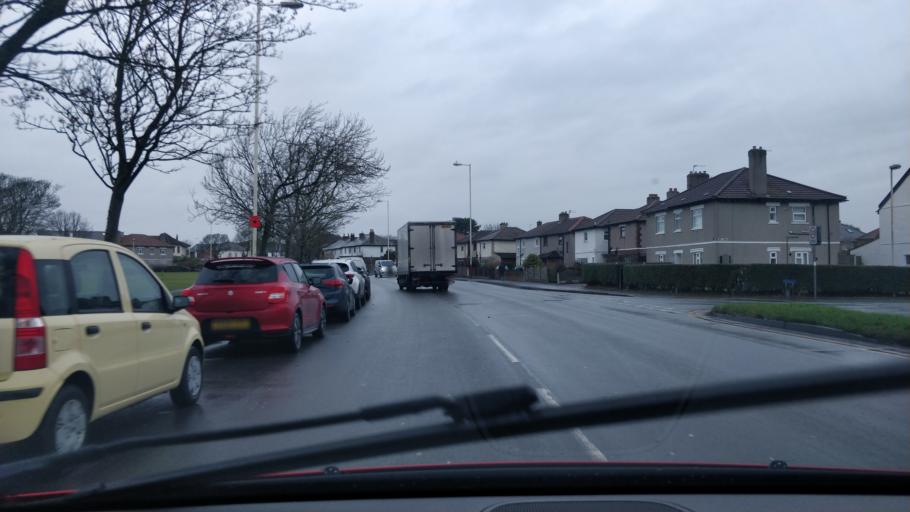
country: GB
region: England
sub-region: Sefton
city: Southport
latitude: 53.6008
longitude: -3.0332
